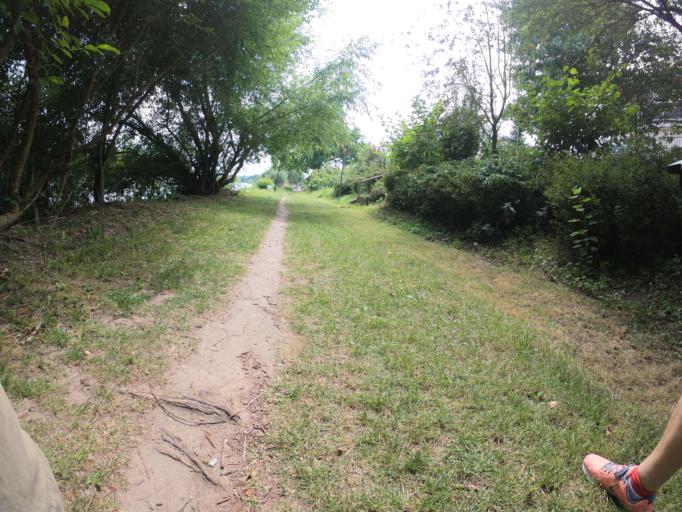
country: DE
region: Bavaria
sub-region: Regierungsbezirk Unterfranken
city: Niedernberg
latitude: 49.9117
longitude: 9.1422
